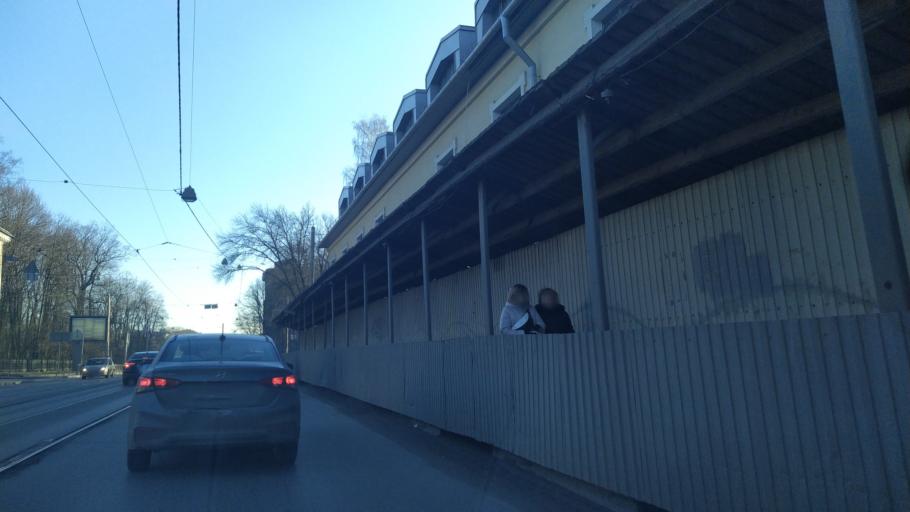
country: RU
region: Leningrad
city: Svetlanovskiy
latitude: 59.9977
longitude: 30.3299
